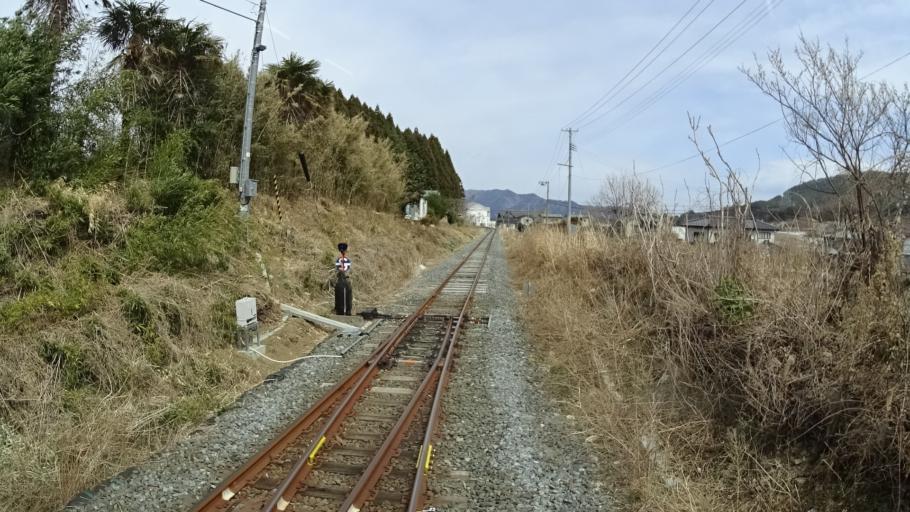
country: JP
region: Iwate
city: Yamada
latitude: 39.4330
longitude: 141.9746
